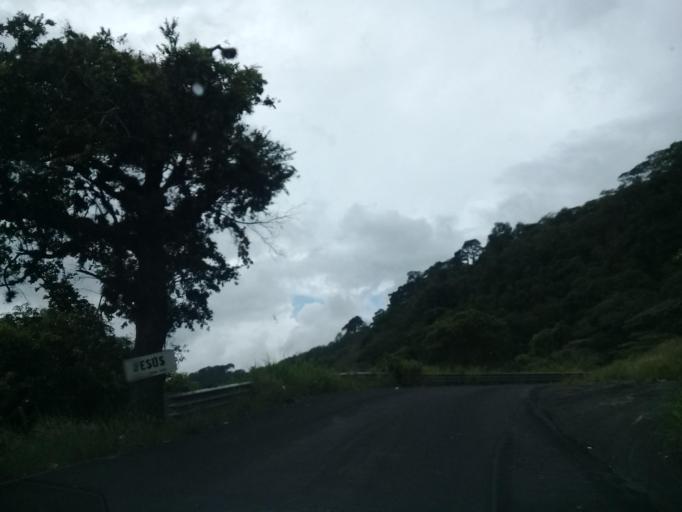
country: MX
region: Veracruz
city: El Castillo
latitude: 19.5581
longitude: -96.8409
